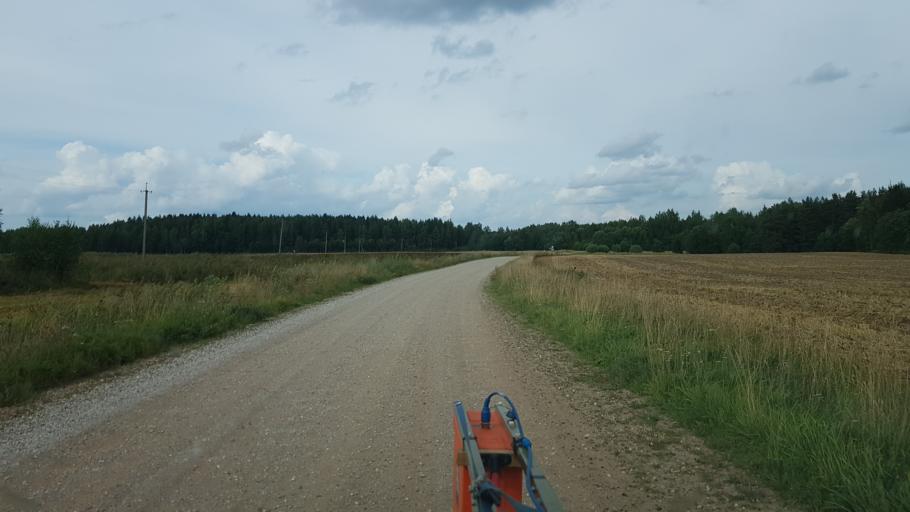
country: RU
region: Pskov
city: Pechory
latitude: 57.8111
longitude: 27.5116
